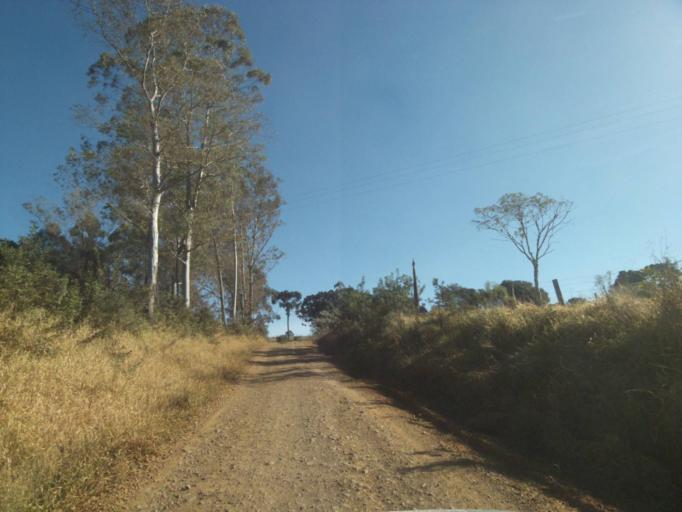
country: BR
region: Parana
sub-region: Tibagi
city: Tibagi
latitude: -24.5412
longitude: -50.5036
